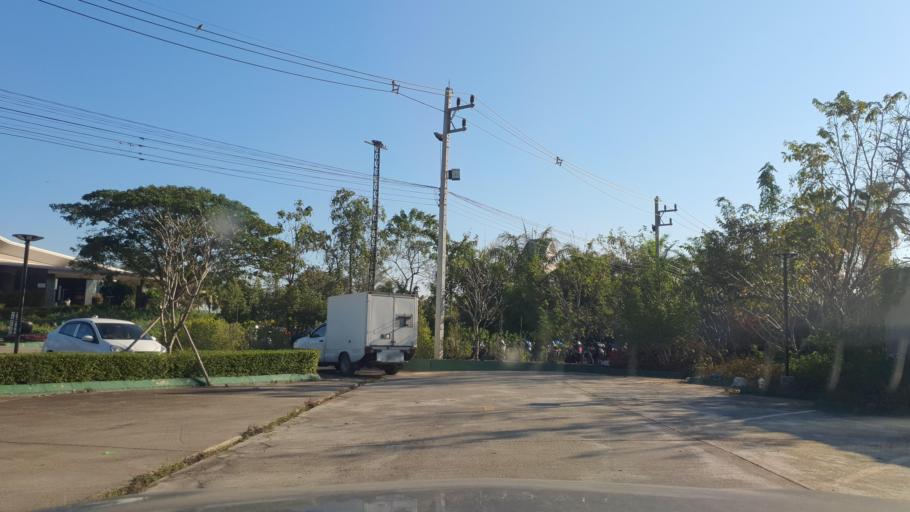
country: TH
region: Chiang Mai
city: Hang Dong
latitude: 18.6947
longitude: 98.9579
